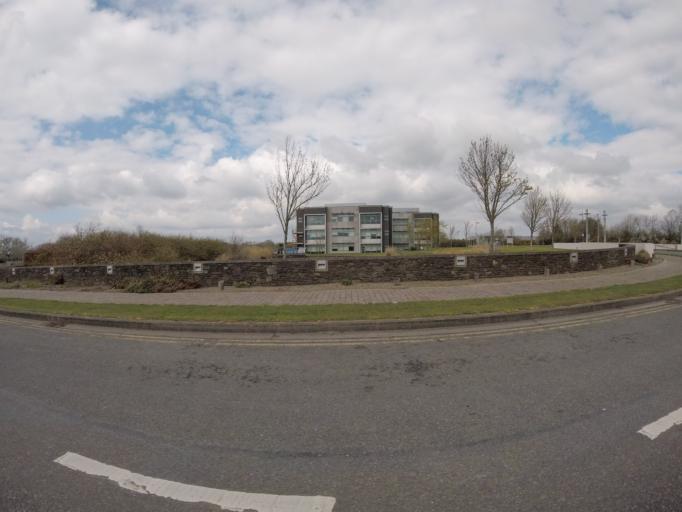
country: IE
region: Munster
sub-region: Waterford
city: Waterford
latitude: 52.2396
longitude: -7.1753
